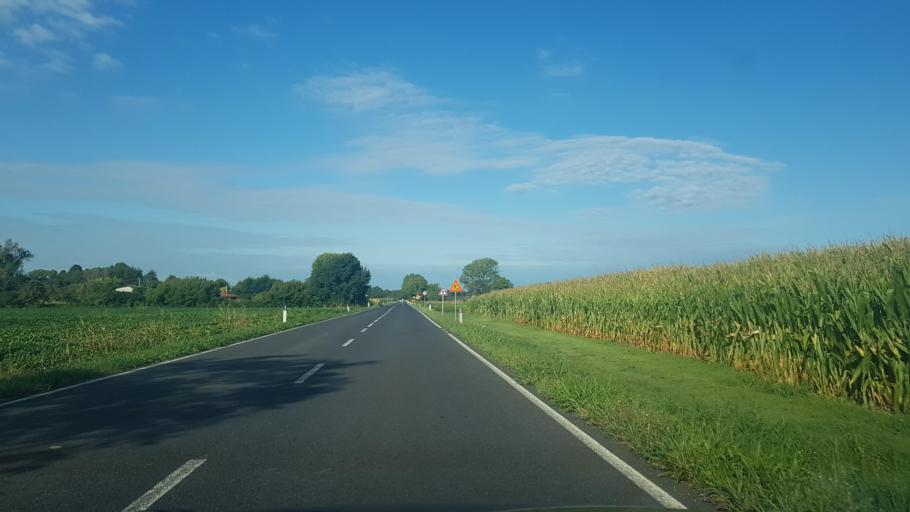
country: IT
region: Friuli Venezia Giulia
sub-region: Provincia di Udine
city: Gonars
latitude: 45.8861
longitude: 13.2466
